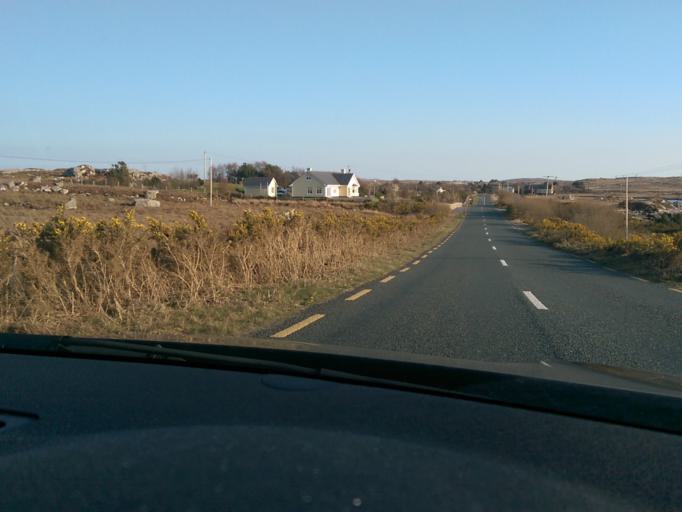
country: IE
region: Connaught
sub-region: County Galway
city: Oughterard
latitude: 53.3821
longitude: -9.5502
